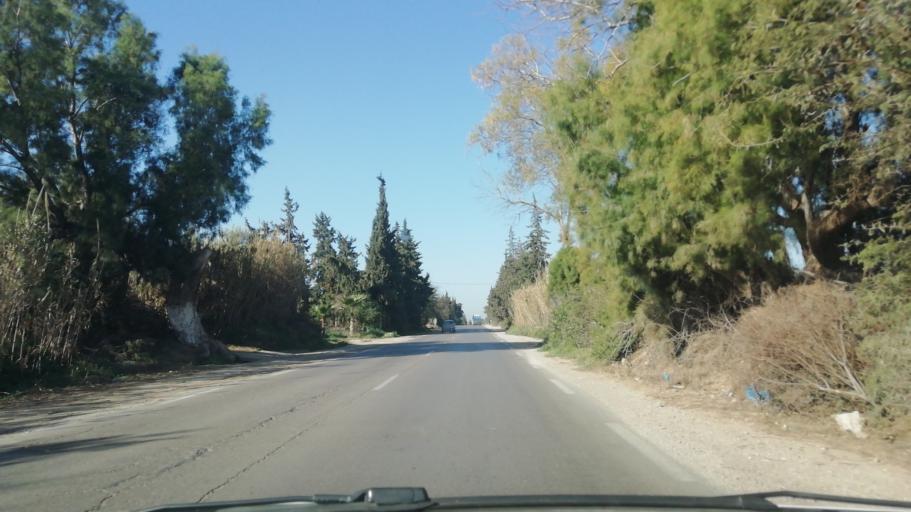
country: DZ
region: Mascara
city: Sig
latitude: 35.5780
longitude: 0.0074
